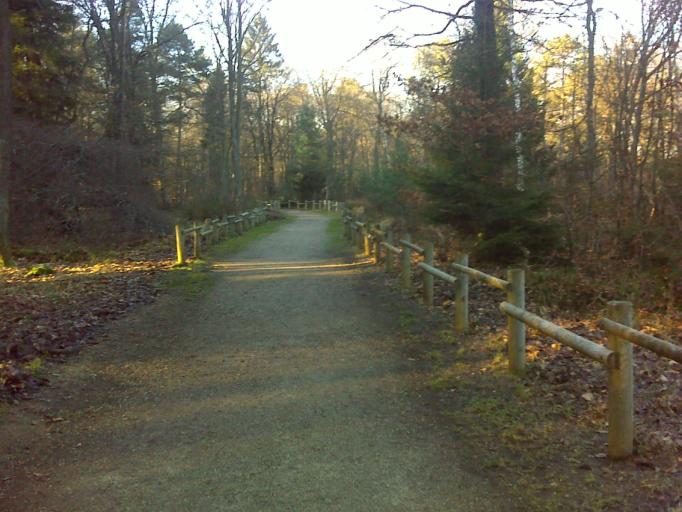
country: FR
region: Champagne-Ardenne
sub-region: Departement de la Marne
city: Verzy
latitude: 49.1341
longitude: 4.1636
